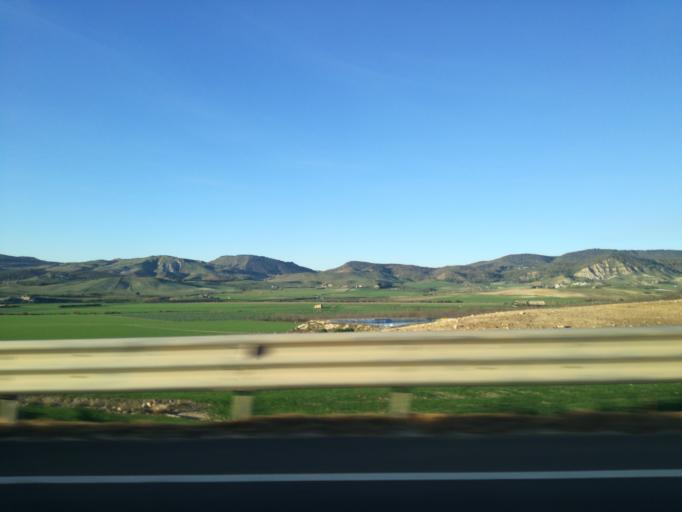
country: IT
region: Sicily
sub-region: Provincia di Caltanissetta
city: Niscemi
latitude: 37.2113
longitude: 14.3978
